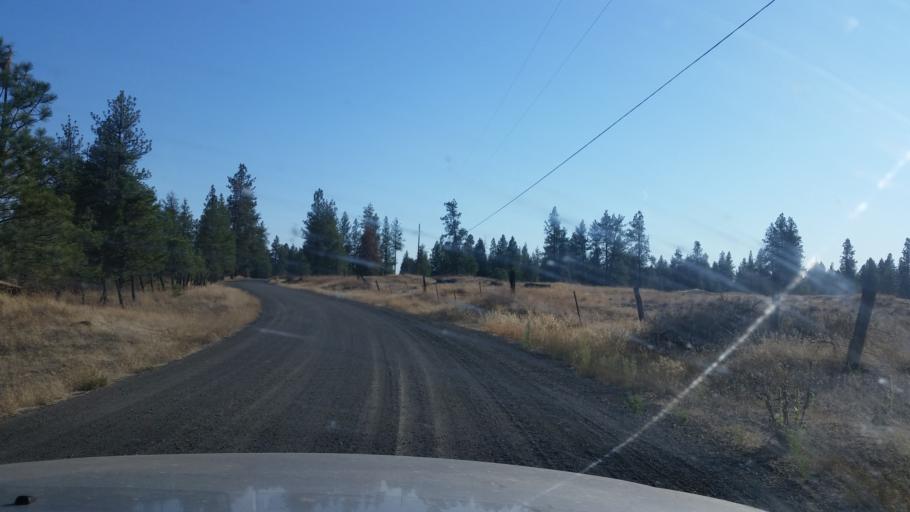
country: US
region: Washington
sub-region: Spokane County
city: Cheney
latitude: 47.4234
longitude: -117.6504
